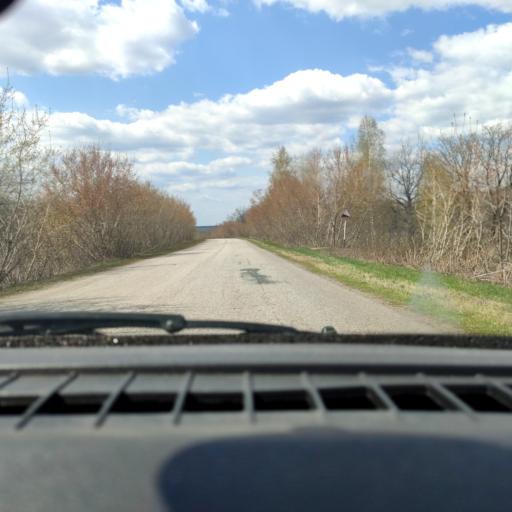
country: RU
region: Samara
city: Krotovka
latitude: 53.5526
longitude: 51.0653
